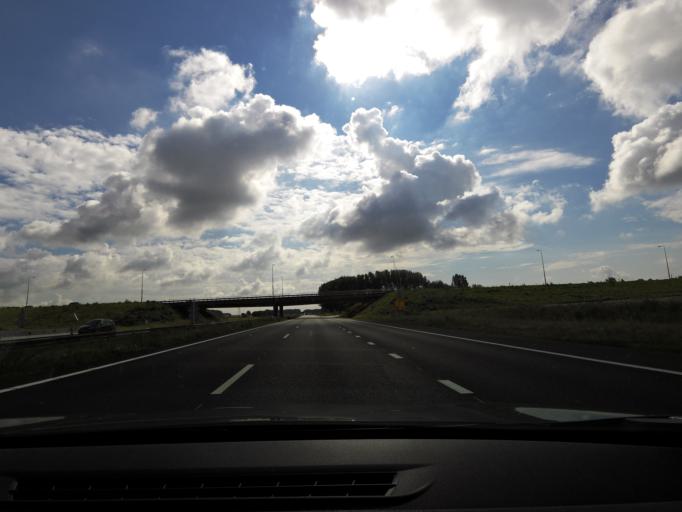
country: NL
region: Zeeland
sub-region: Gemeente Borsele
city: Borssele
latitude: 51.4889
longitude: 3.7941
